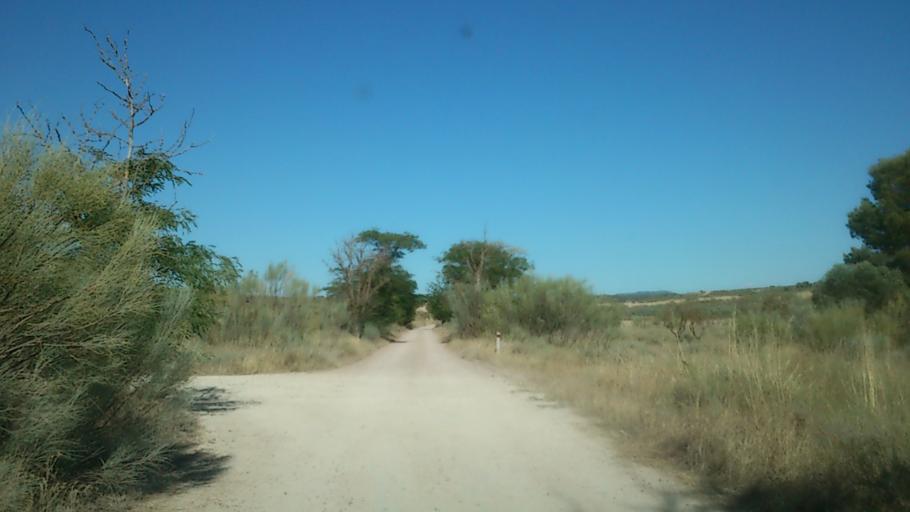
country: ES
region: Aragon
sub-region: Provincia de Zaragoza
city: San Mateo de Gallego
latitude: 41.7681
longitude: -0.7524
